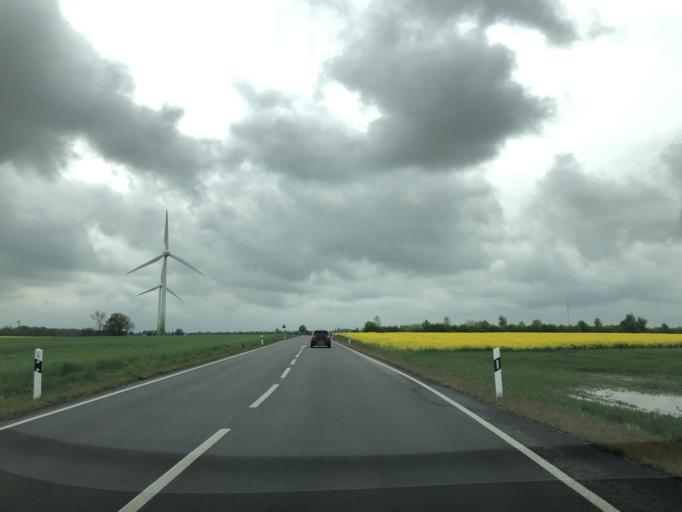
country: DE
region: Brandenburg
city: Gerdshagen
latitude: 53.2269
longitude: 12.2049
